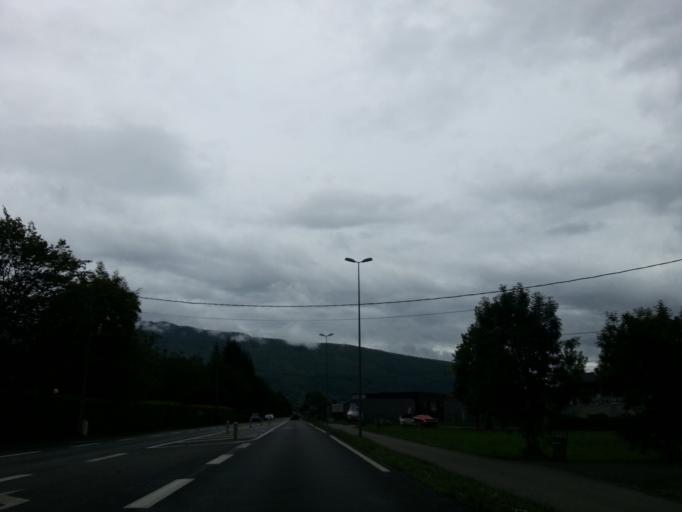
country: FR
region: Rhone-Alpes
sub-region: Departement de la Haute-Savoie
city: Saint-Jorioz
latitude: 45.8302
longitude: 6.1821
